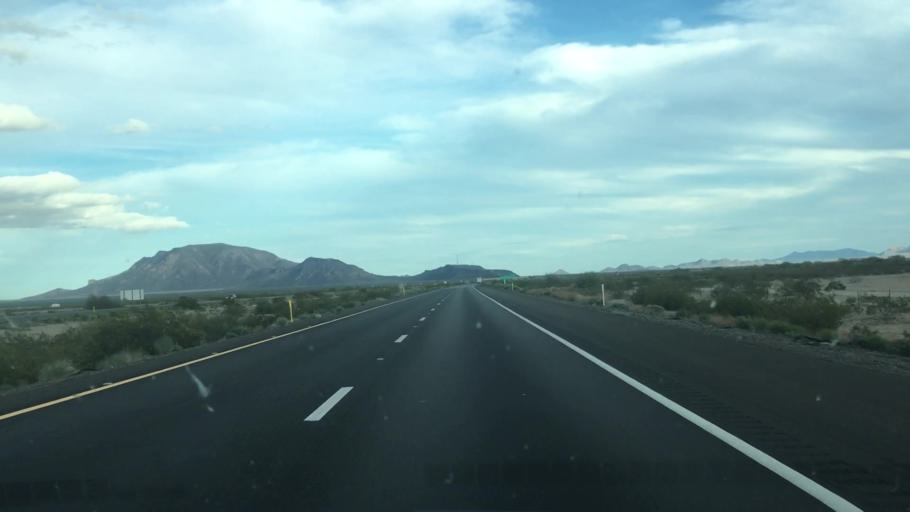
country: US
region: Arizona
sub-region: La Paz County
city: Salome
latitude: 33.5421
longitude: -113.1783
